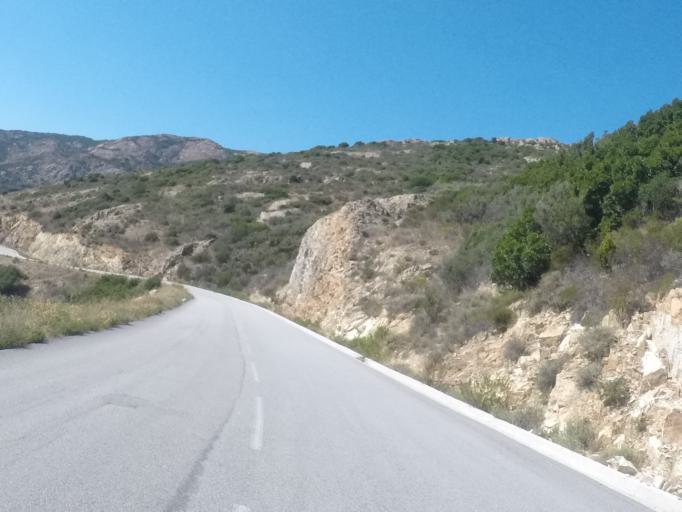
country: FR
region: Corsica
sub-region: Departement de la Haute-Corse
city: Calvi
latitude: 42.4763
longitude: 8.7549
